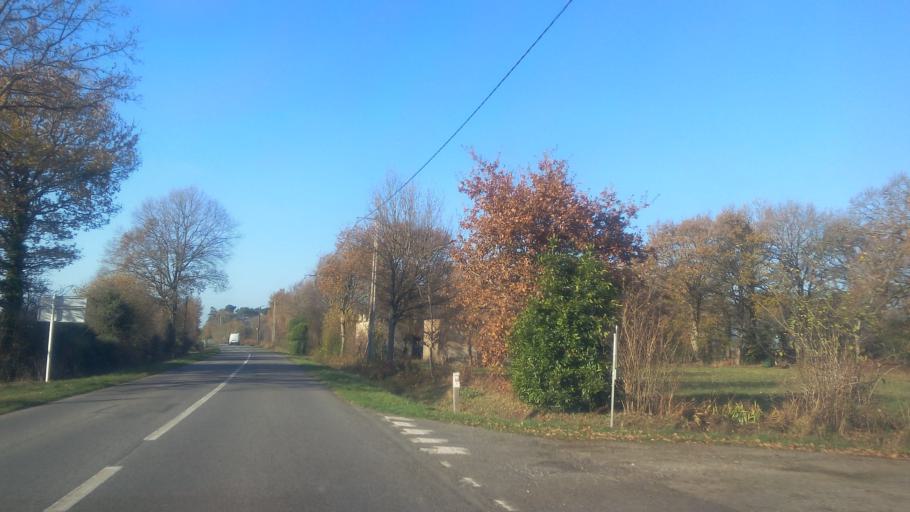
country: FR
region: Brittany
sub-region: Departement du Morbihan
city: Peillac
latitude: 47.7145
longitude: -2.1877
